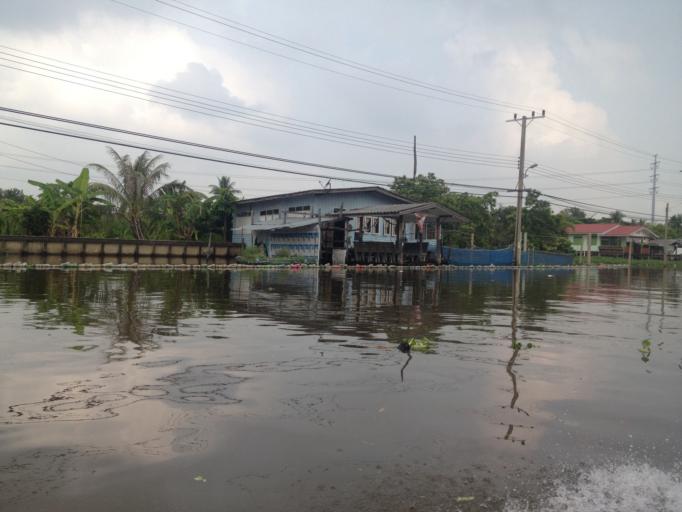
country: TH
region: Nonthaburi
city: Bang Kruai
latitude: 13.7968
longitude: 100.4703
